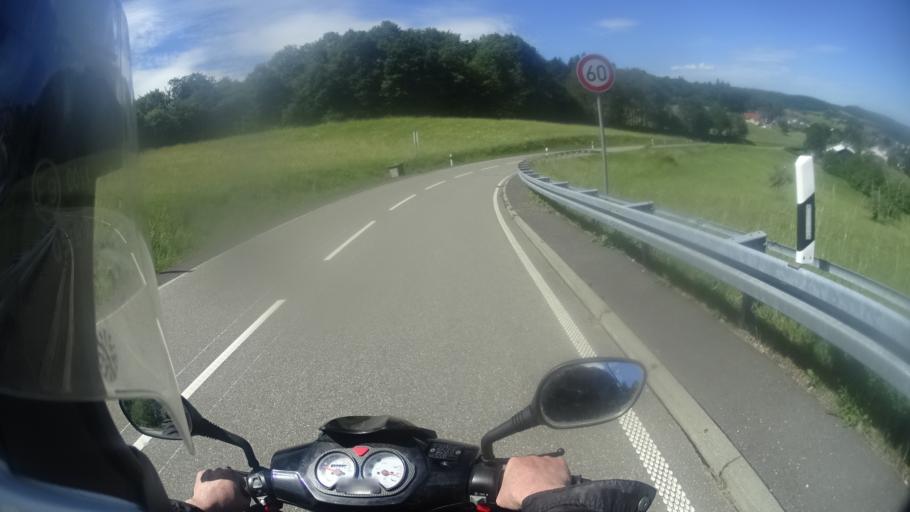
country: DE
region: Hesse
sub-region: Regierungsbezirk Darmstadt
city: Schlangenbad
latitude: 50.0975
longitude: 8.0679
